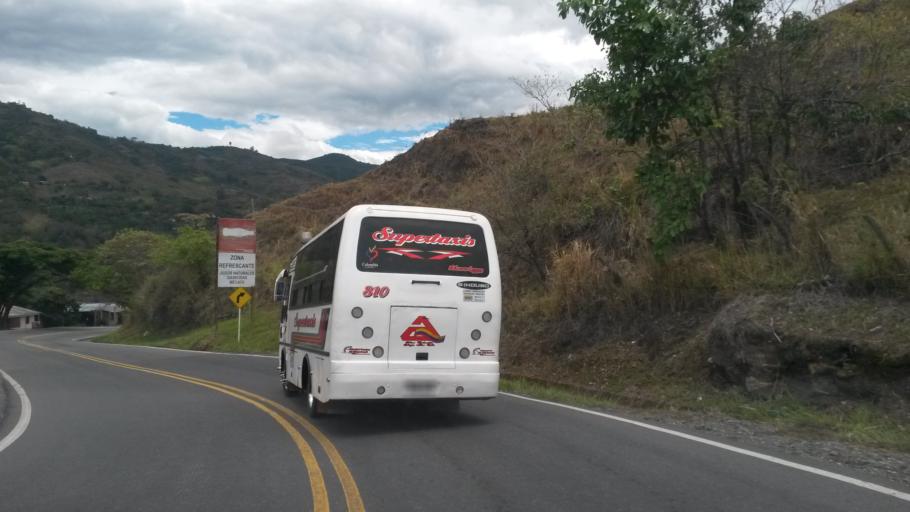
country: CO
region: Cauca
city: Rosas
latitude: 2.2814
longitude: -76.7186
